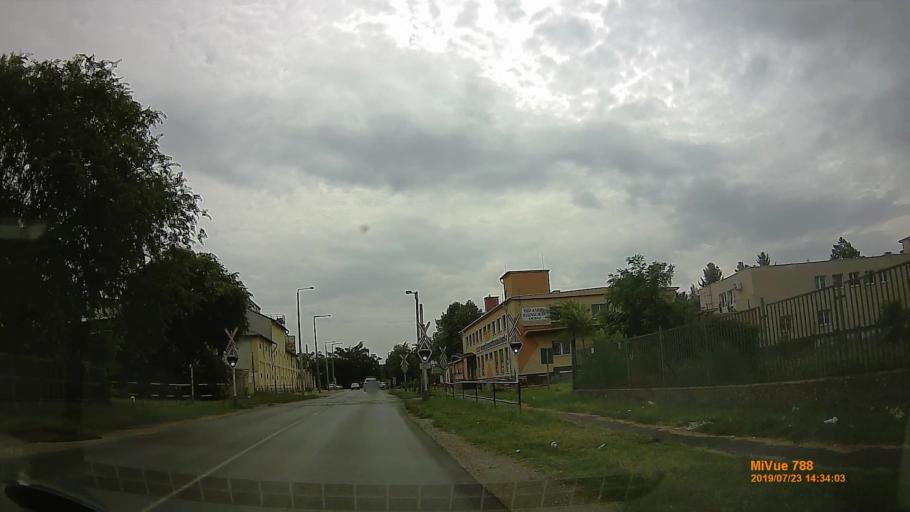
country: HU
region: Szabolcs-Szatmar-Bereg
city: Nyiregyhaza
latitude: 47.9386
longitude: 21.7128
